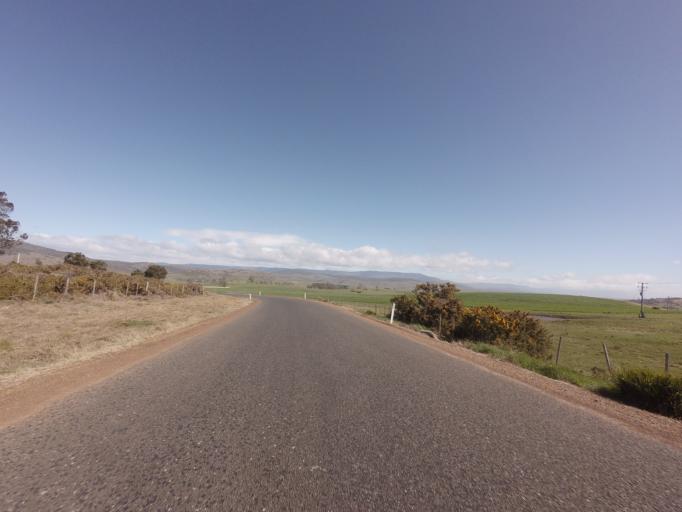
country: AU
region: Tasmania
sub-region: Northern Midlands
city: Evandale
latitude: -41.8960
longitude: 147.4080
